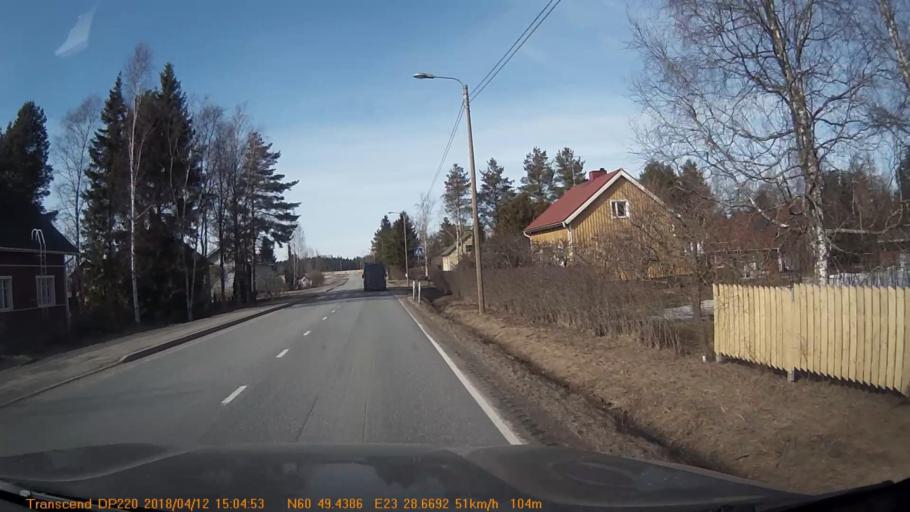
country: FI
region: Haeme
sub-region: Forssa
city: Jokioinen
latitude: 60.8241
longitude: 23.4778
